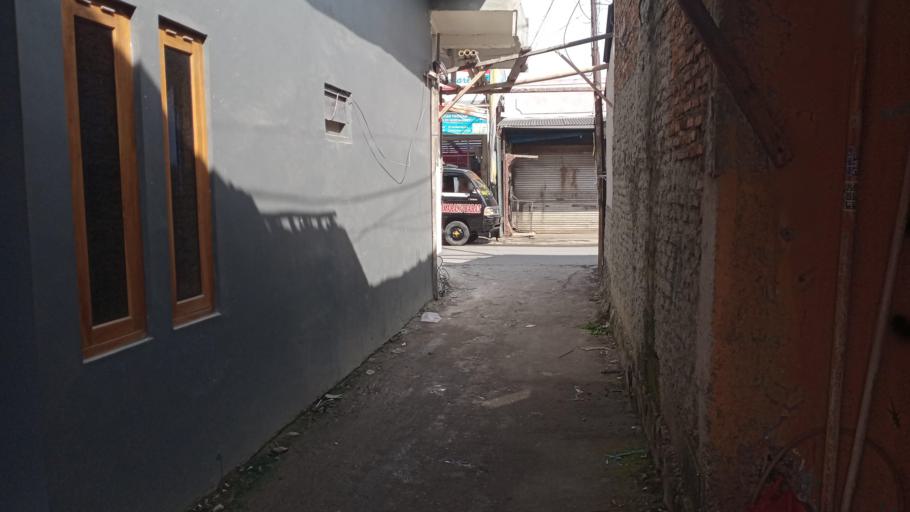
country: ID
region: West Java
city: Cikarang
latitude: -6.2639
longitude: 107.1156
